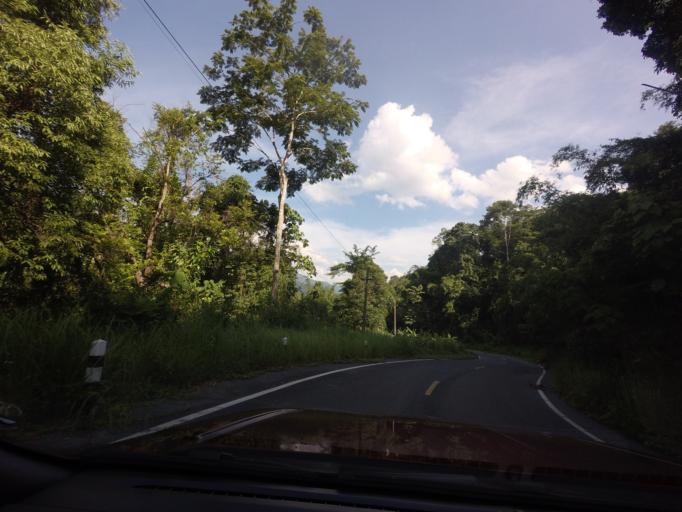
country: TH
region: Yala
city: Than To
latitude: 6.0714
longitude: 101.3649
